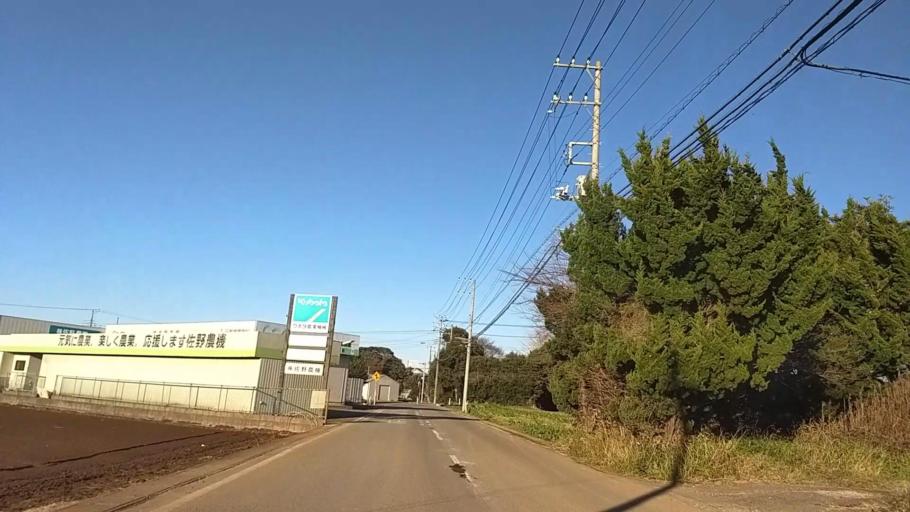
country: JP
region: Chiba
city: Asahi
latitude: 35.7340
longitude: 140.7390
